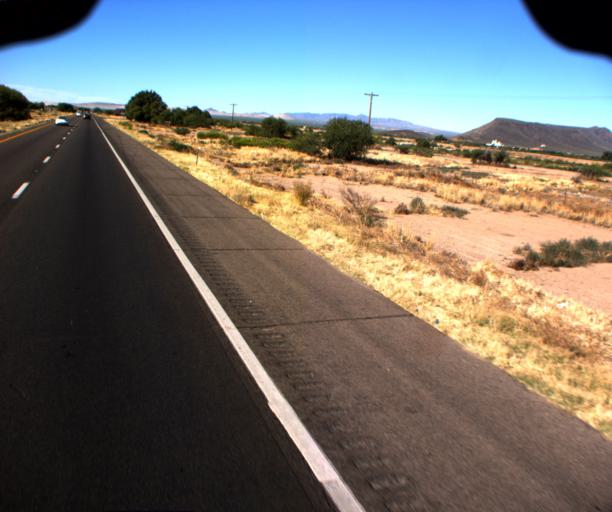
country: US
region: Arizona
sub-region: Pima County
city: Drexel Heights
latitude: 32.1188
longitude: -110.9894
